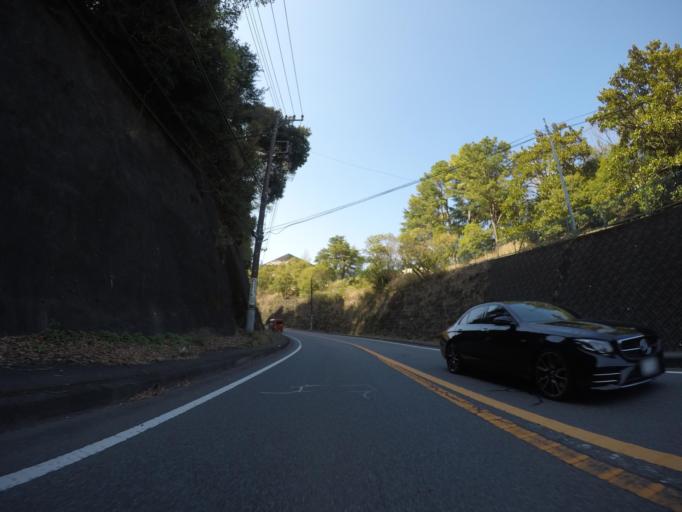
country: JP
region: Shizuoka
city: Mishima
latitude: 35.0416
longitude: 138.9230
